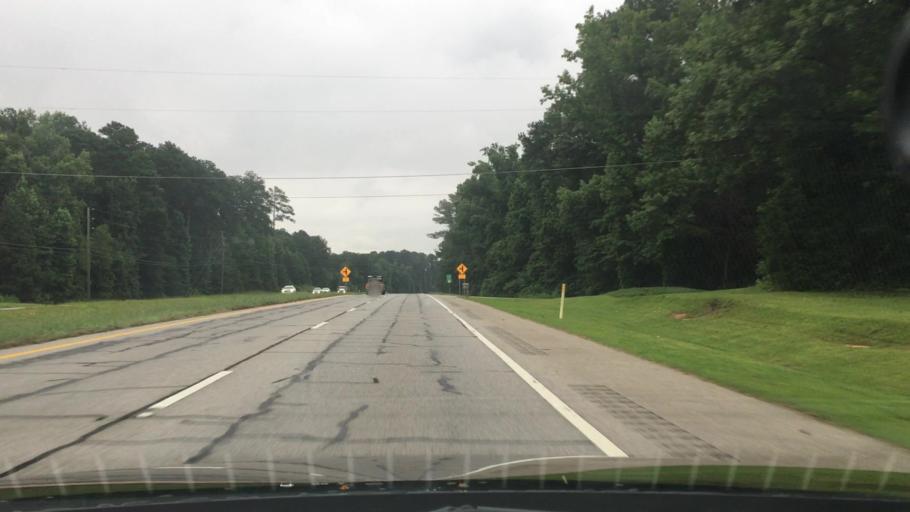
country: US
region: Georgia
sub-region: Fayette County
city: Peachtree City
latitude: 33.4017
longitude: -84.6377
